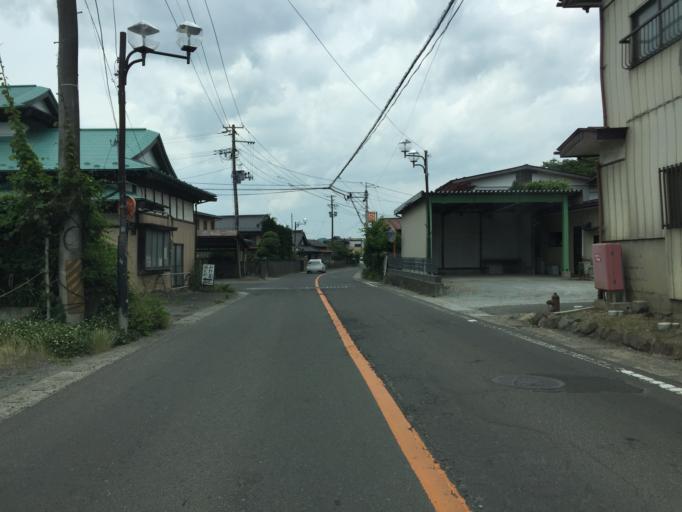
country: JP
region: Miyagi
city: Marumori
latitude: 37.8671
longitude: 140.8263
